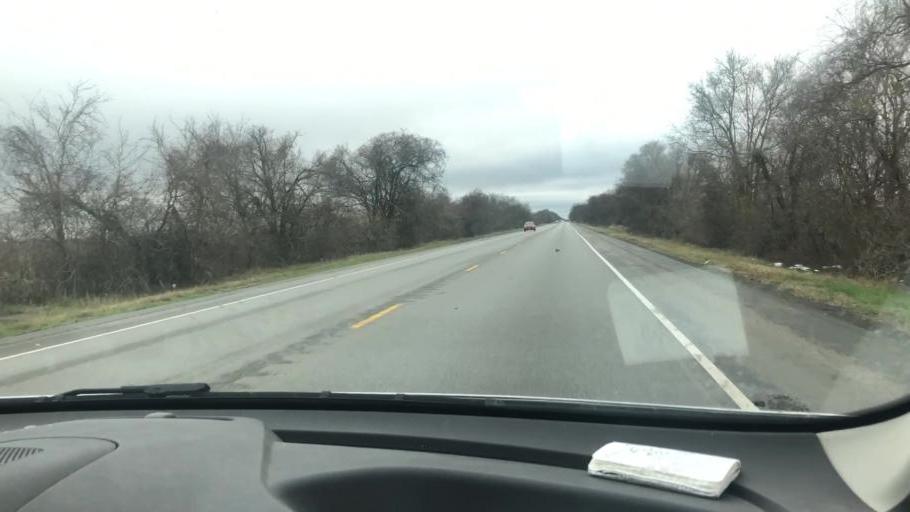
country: US
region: Texas
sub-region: Matagorda County
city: Van Vleck
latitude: 29.1163
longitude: -95.9801
